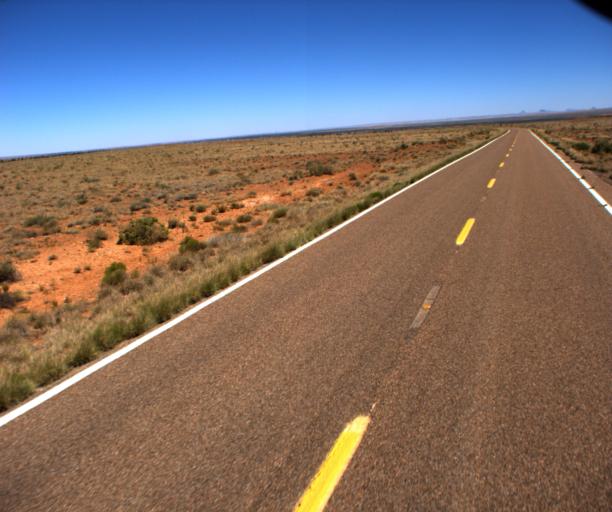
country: US
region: Arizona
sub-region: Navajo County
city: Winslow
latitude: 34.9123
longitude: -110.6386
